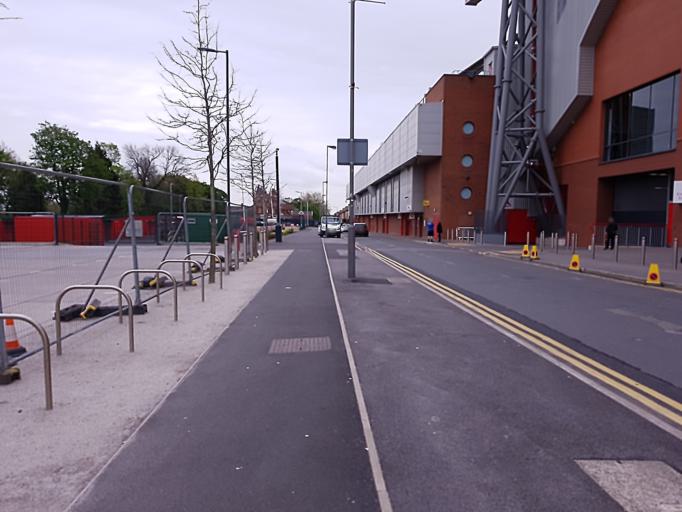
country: GB
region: England
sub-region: Liverpool
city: Liverpool
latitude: 53.4321
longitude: -2.9613
